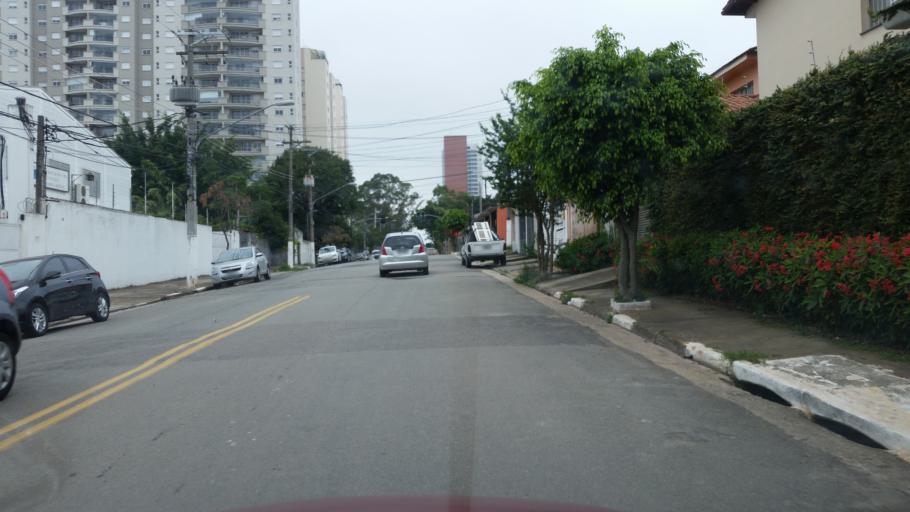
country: BR
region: Sao Paulo
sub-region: Diadema
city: Diadema
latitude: -23.6361
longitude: -46.6628
